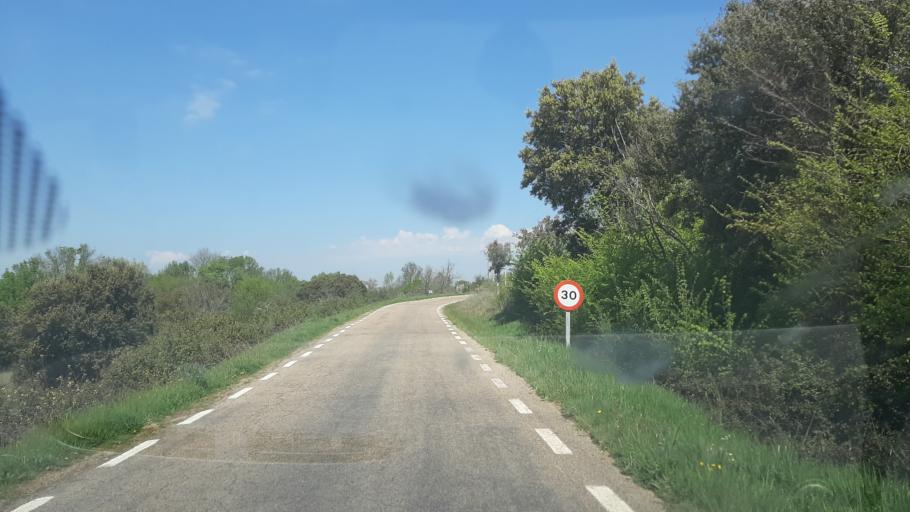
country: ES
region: Castille and Leon
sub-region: Provincia de Salamanca
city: Tejeda y Segoyuela
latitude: 40.6263
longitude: -6.0225
